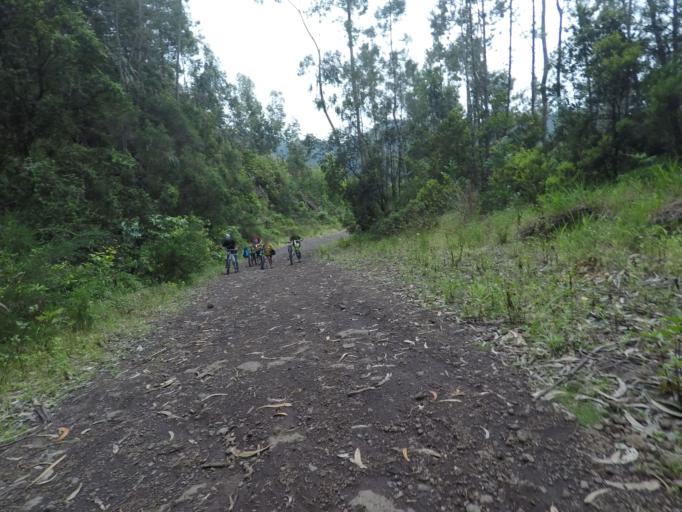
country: PT
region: Madeira
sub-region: Sao Vicente
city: Sao Vicente
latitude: 32.7771
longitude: -17.0516
